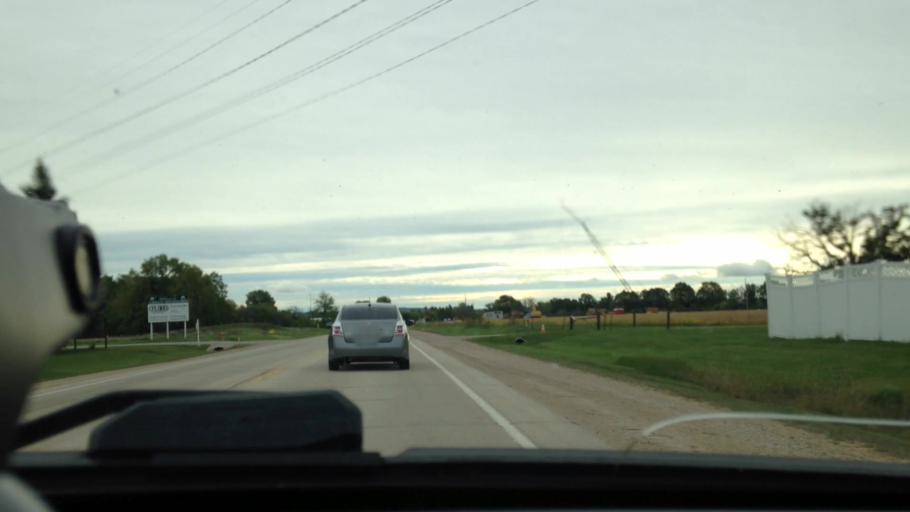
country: US
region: Wisconsin
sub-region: Fond du Lac County
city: North Fond du Lac
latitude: 43.8000
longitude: -88.4937
